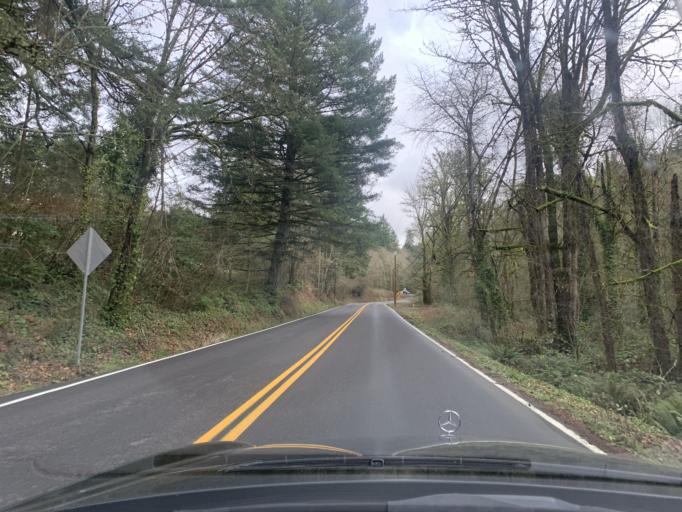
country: US
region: Oregon
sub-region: Multnomah County
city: Gresham
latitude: 45.4706
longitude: -122.4517
